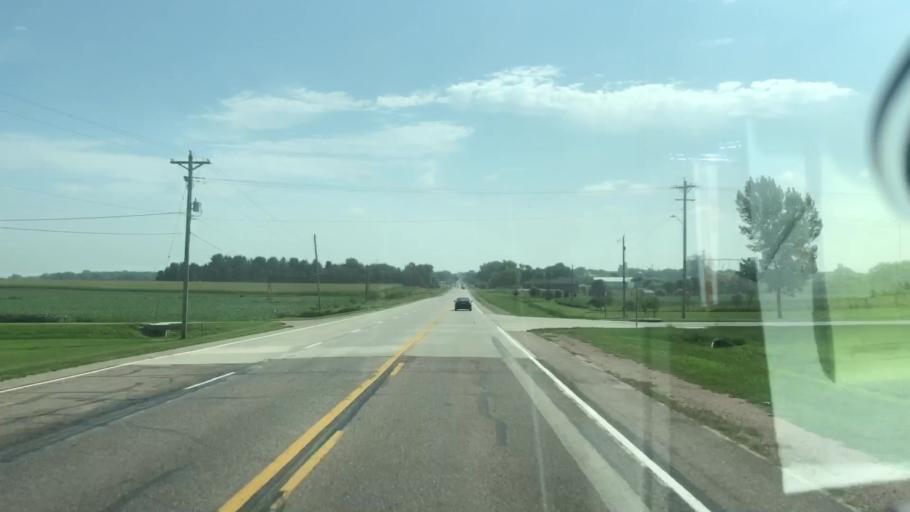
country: US
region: Iowa
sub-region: O'Brien County
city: Sheldon
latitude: 43.1859
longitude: -95.8777
